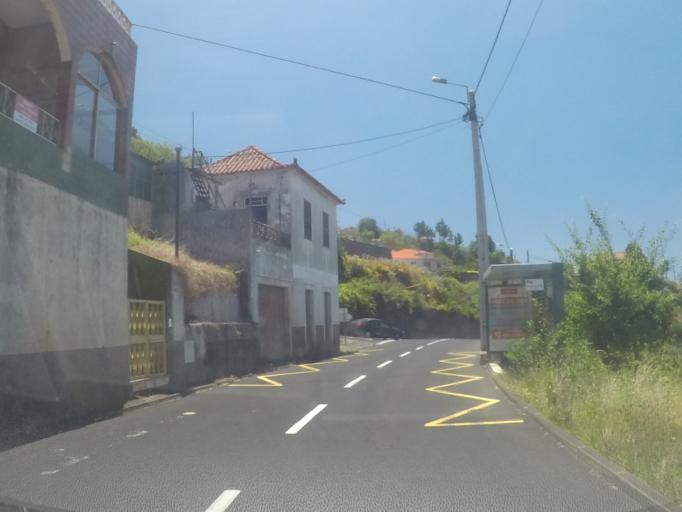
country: PT
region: Madeira
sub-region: Camara de Lobos
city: Curral das Freiras
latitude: 32.6879
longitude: -16.9933
